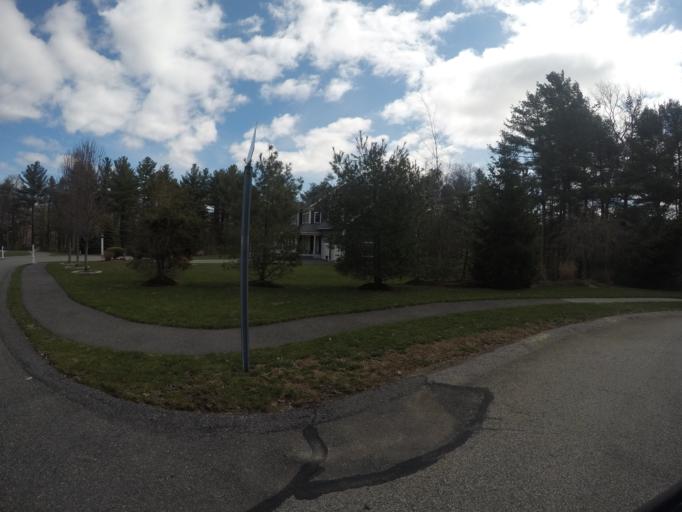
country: US
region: Massachusetts
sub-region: Bristol County
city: Easton
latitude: 42.0713
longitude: -71.1178
